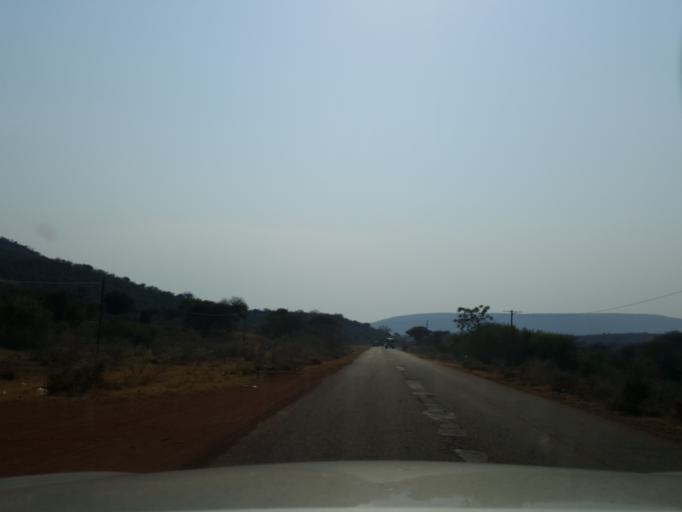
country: BW
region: South East
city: Lobatse
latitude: -25.3051
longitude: 25.8197
